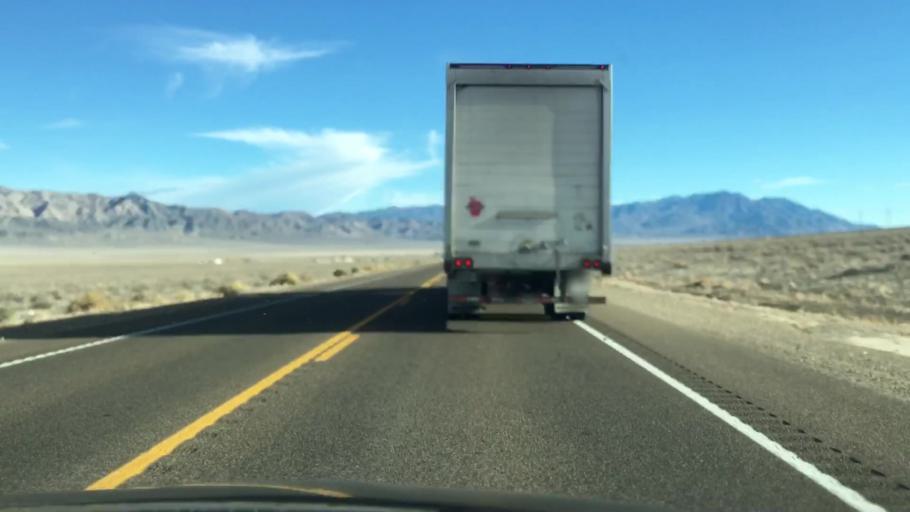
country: US
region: Nevada
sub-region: Mineral County
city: Hawthorne
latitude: 38.5210
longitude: -118.2096
